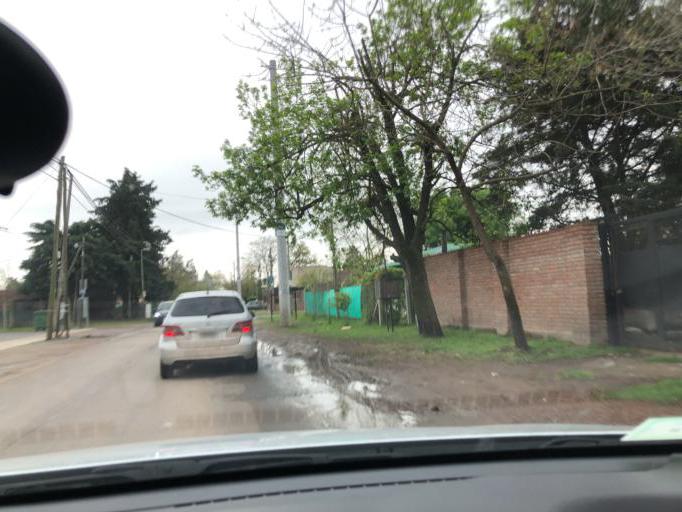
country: AR
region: Buenos Aires
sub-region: Partido de La Plata
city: La Plata
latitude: -34.8959
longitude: -58.0665
